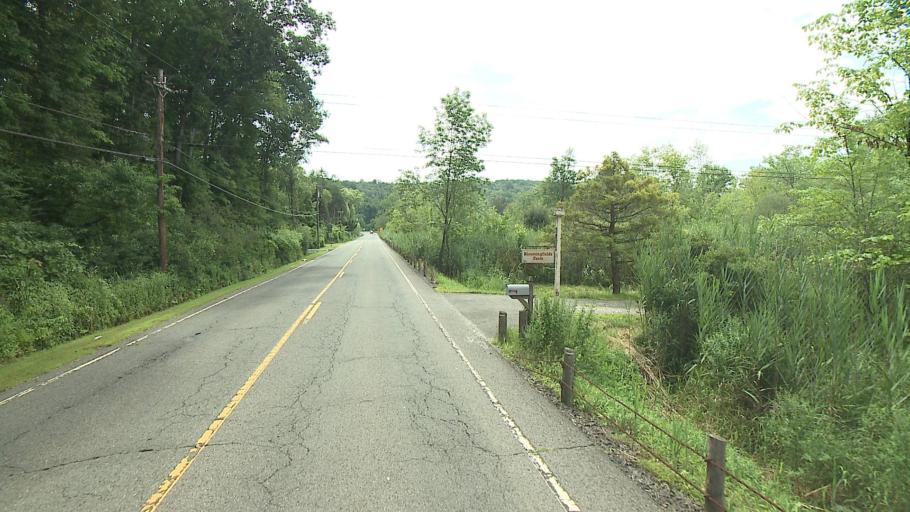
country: US
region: Connecticut
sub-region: Fairfield County
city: Sherman
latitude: 41.6413
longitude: -73.5009
